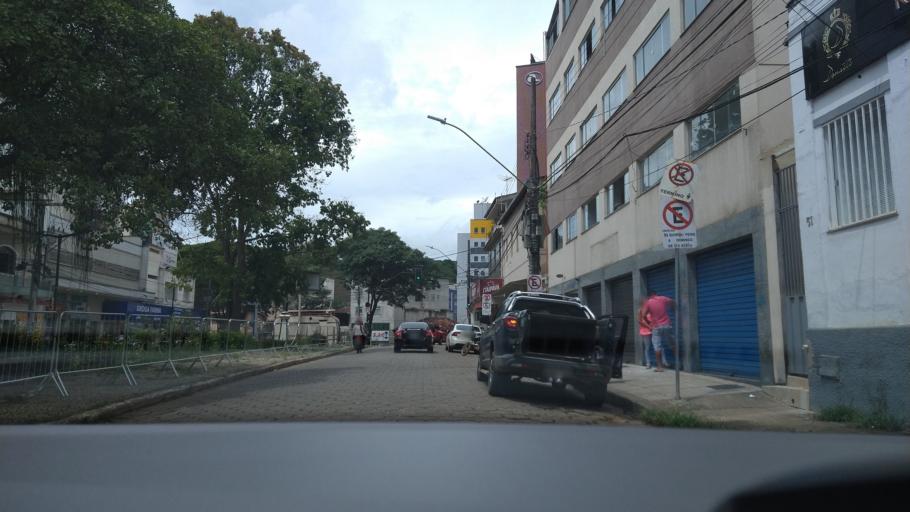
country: BR
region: Minas Gerais
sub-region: Vicosa
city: Vicosa
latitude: -20.7570
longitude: -42.8781
